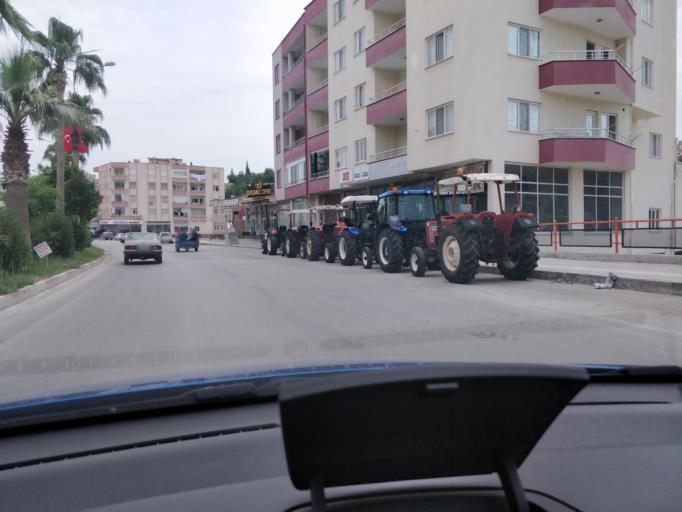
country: TR
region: Mersin
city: Mut
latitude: 36.6458
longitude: 33.4303
